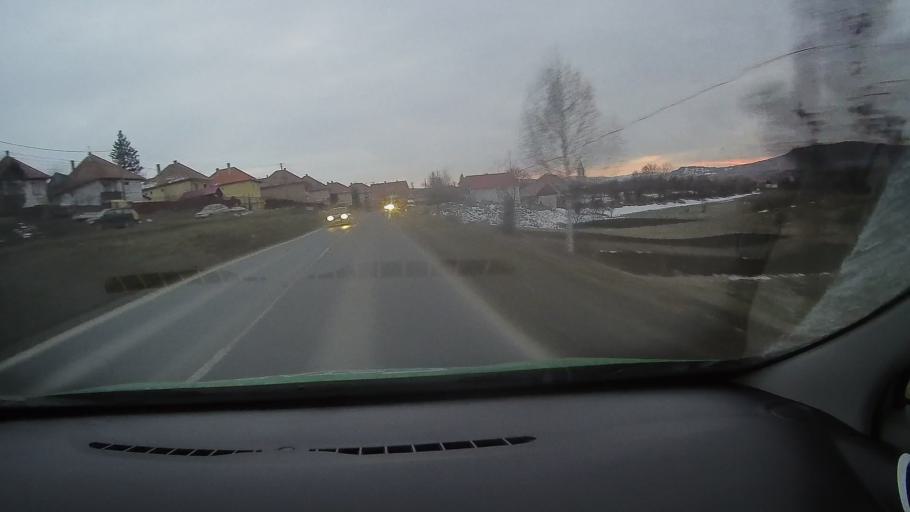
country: RO
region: Harghita
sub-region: Comuna Feliceni
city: Feliceni
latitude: 46.2762
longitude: 25.2851
